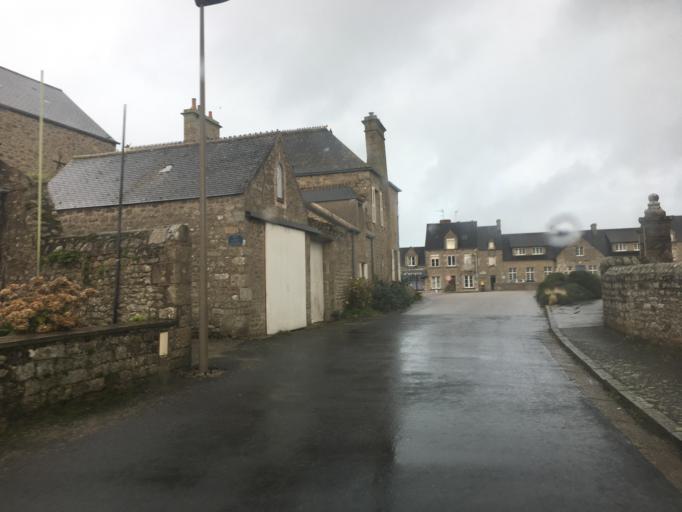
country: FR
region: Lower Normandy
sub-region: Departement de la Manche
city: Reville
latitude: 49.6861
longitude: -1.2831
